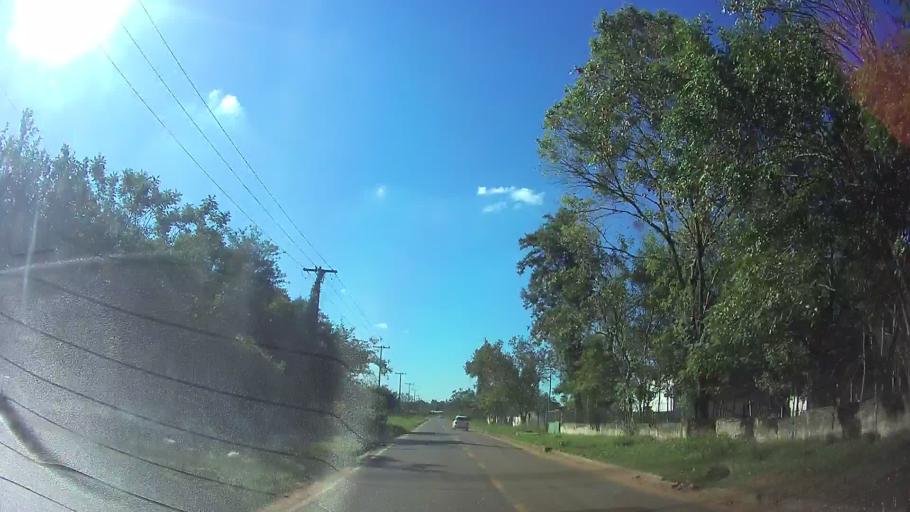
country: PY
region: Central
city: Limpio
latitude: -25.1955
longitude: -57.4771
